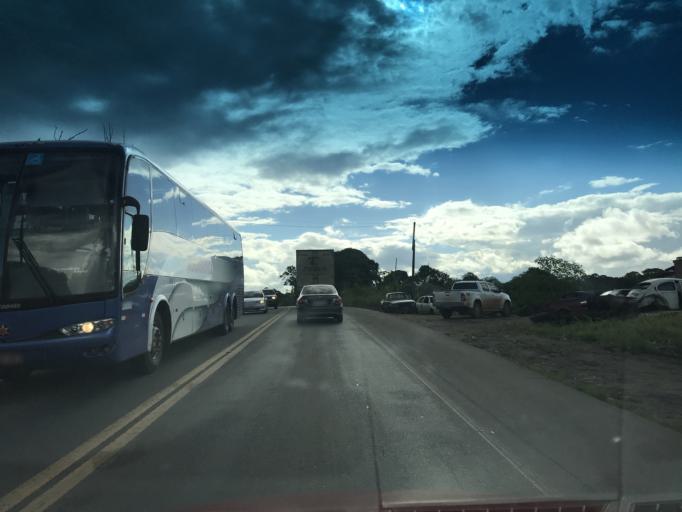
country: BR
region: Bahia
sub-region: Ibirapitanga
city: Ibirapitanga
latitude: -14.1506
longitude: -39.3335
